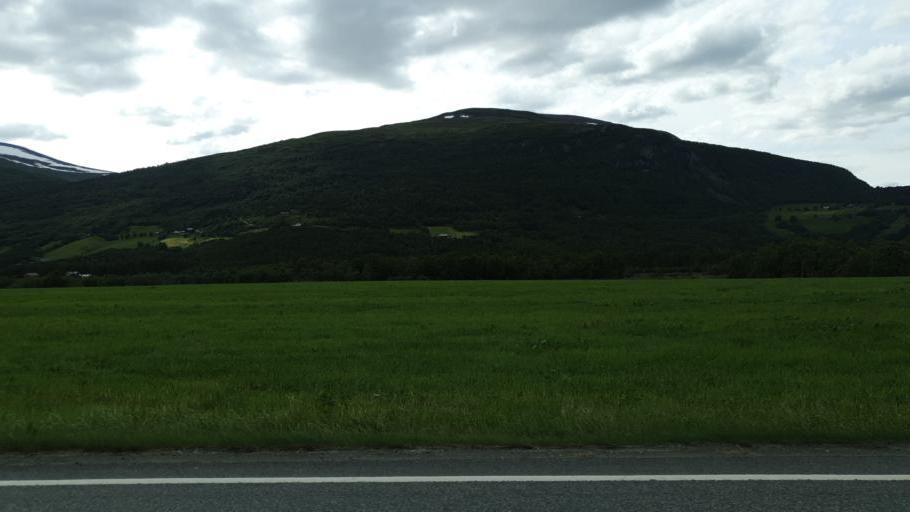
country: NO
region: Sor-Trondelag
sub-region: Oppdal
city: Oppdal
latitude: 62.5448
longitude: 9.6311
